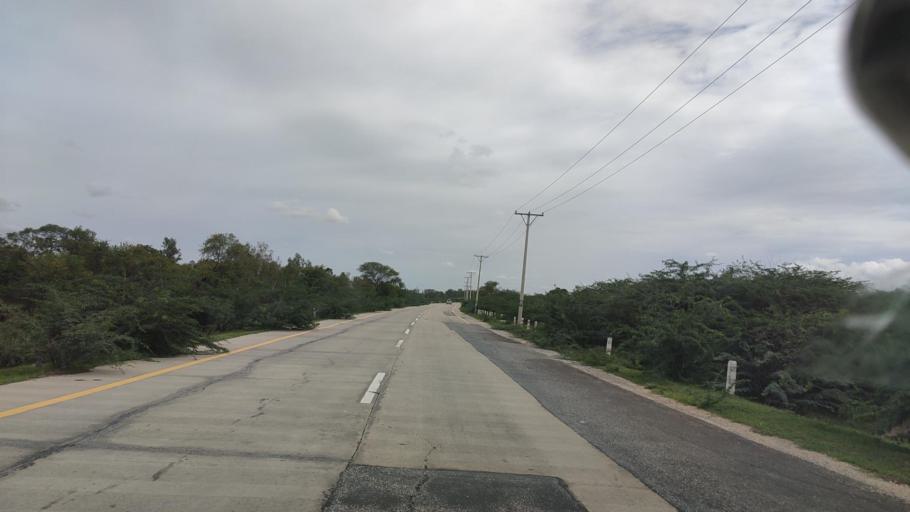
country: MM
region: Mandalay
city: Meiktila
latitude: 21.1332
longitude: 96.0276
